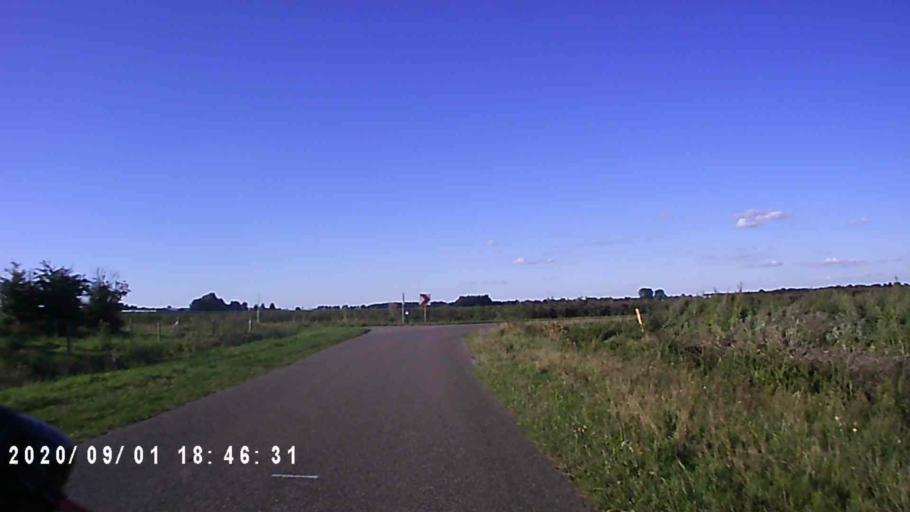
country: NL
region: Groningen
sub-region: Gemeente Veendam
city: Veendam
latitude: 53.1477
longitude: 6.8475
